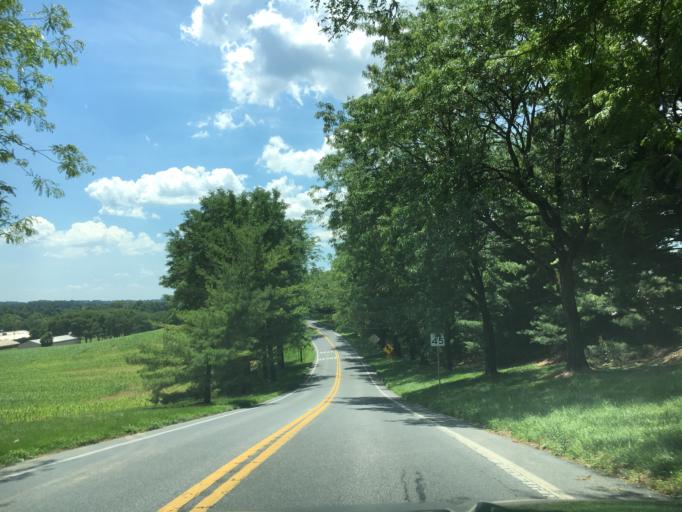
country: US
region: Pennsylvania
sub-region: Lehigh County
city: Schnecksville
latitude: 40.6602
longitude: -75.5761
